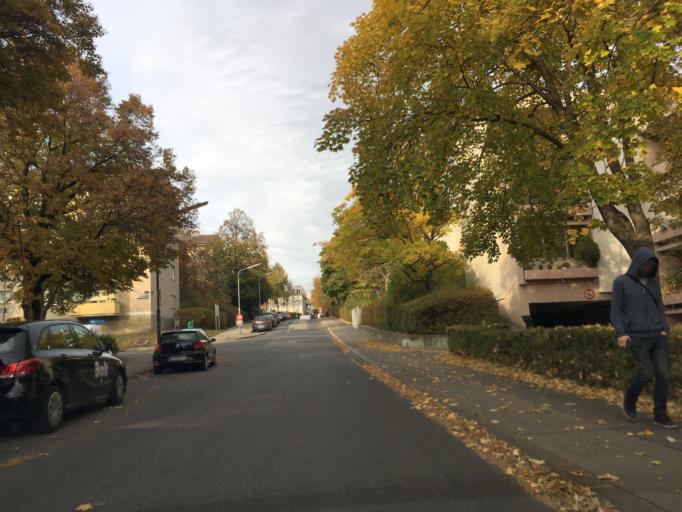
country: AT
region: Vienna
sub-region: Wien Stadt
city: Vienna
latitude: 48.2433
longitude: 16.3288
